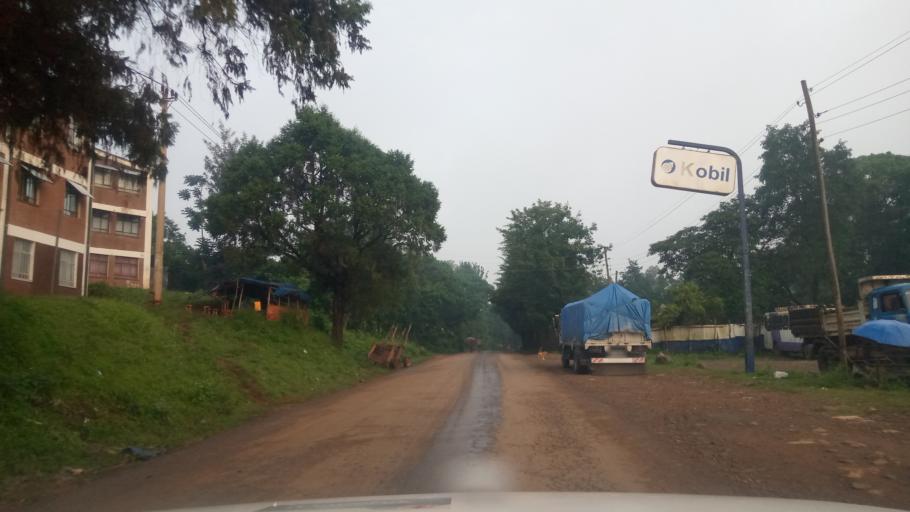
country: ET
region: Oromiya
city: Jima
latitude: 7.6876
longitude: 36.8291
